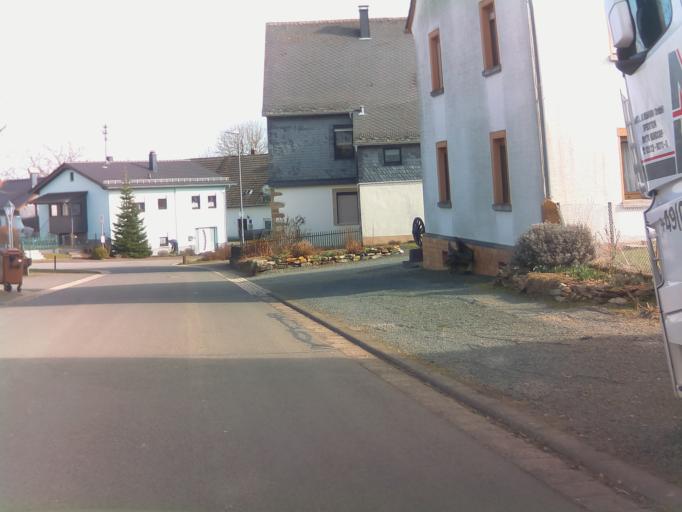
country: DE
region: Rheinland-Pfalz
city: Buhlenberg
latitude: 49.6557
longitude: 7.1191
